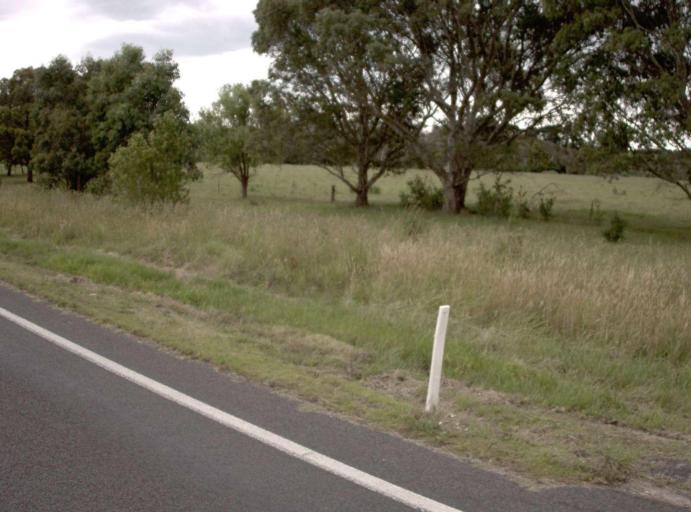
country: AU
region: Victoria
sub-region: Wellington
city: Sale
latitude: -38.2952
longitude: 147.0343
